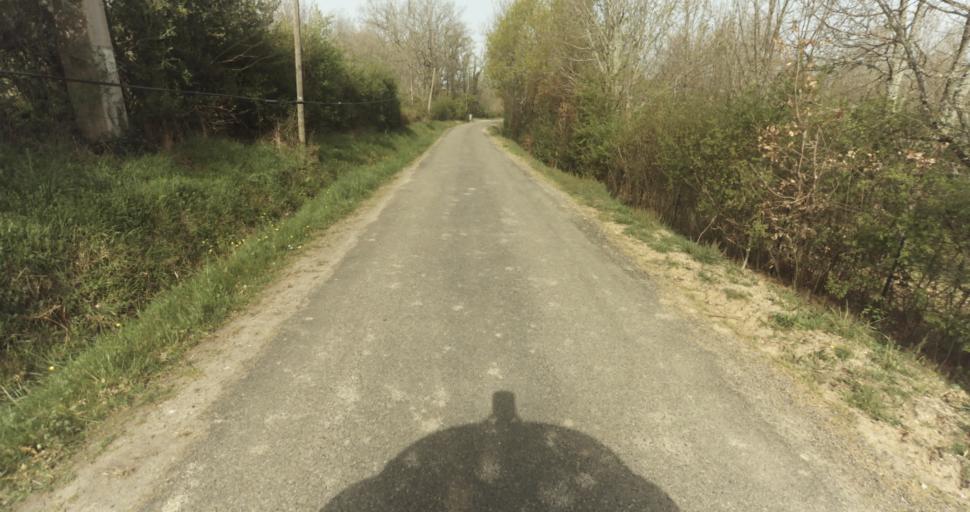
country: FR
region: Midi-Pyrenees
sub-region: Departement du Tarn-et-Garonne
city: Moissac
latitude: 44.1451
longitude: 1.0822
